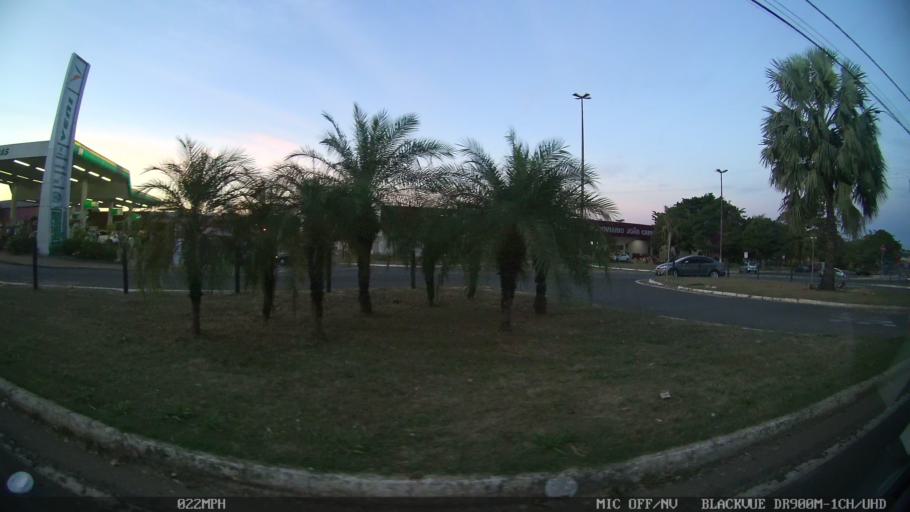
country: BR
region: Sao Paulo
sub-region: Catanduva
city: Catanduva
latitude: -21.1255
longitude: -48.9850
